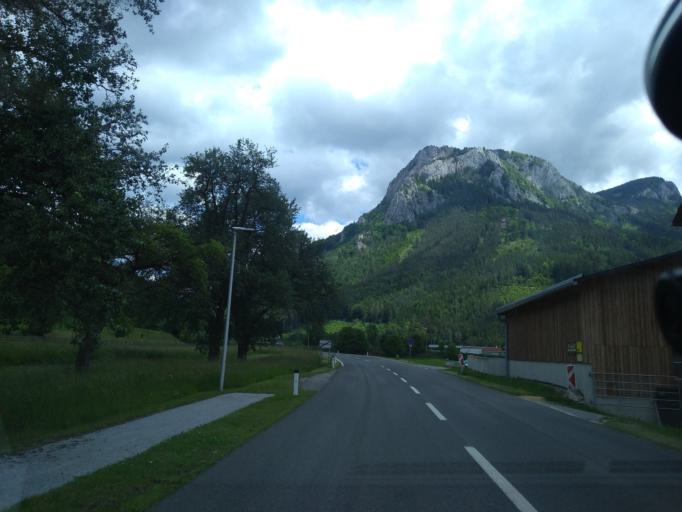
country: AT
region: Styria
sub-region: Politischer Bezirk Graz-Umgebung
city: Rothelstein
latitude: 47.3103
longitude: 15.3708
